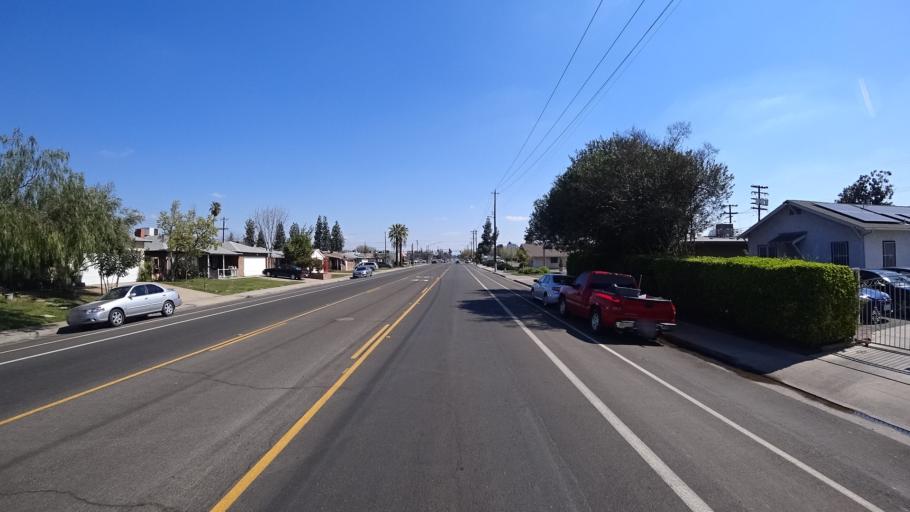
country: US
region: California
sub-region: Fresno County
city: Fresno
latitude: 36.8013
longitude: -119.7836
